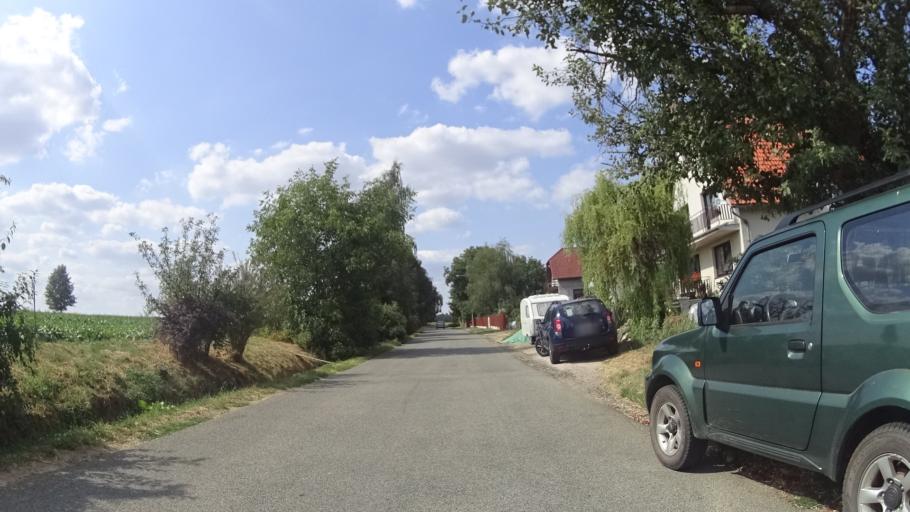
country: CZ
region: Kralovehradecky
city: Liban
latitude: 50.4079
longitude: 15.2671
